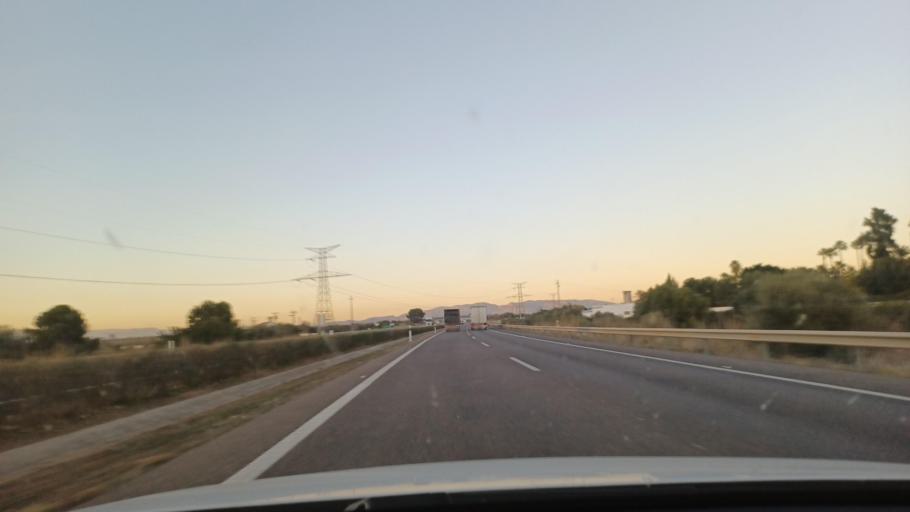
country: ES
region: Valencia
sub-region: Provincia de Castello
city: Alquerias del Nino Perdido
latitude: 39.9294
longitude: -0.1356
